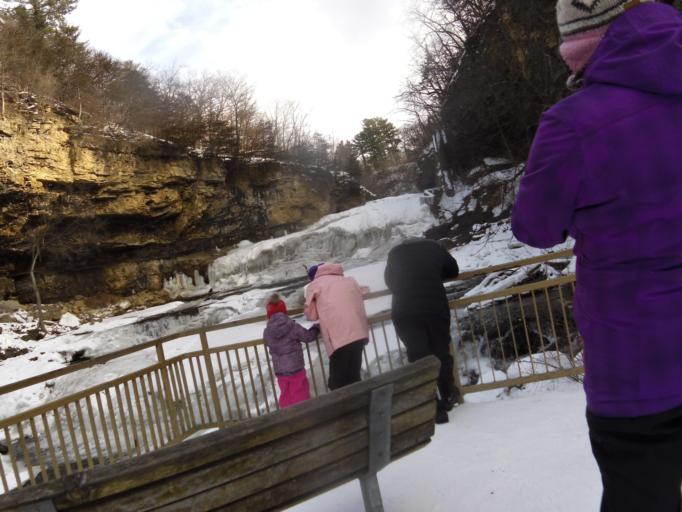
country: US
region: Wisconsin
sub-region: Saint Croix County
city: North Hudson
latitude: 45.0239
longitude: -92.6642
